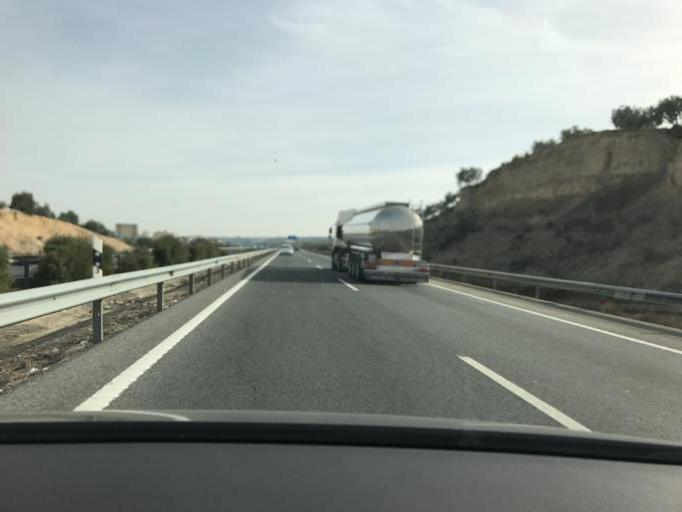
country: ES
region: Andalusia
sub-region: Provincia de Granada
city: Moraleda de Zafayona
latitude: 37.1795
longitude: -3.9148
